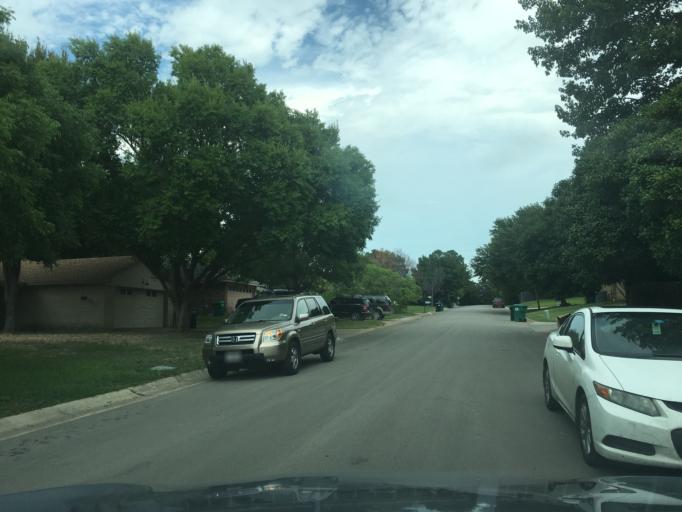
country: US
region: Texas
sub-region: Denton County
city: Denton
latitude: 33.1939
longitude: -97.1580
